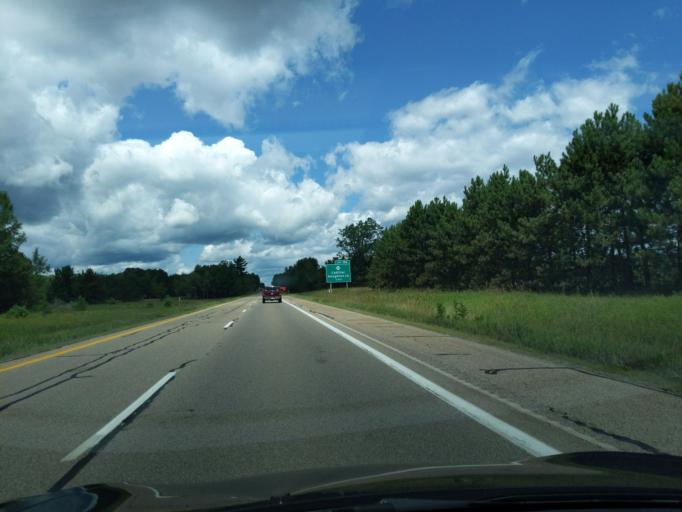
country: US
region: Michigan
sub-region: Roscommon County
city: Houghton Lake
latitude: 44.3142
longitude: -84.8057
